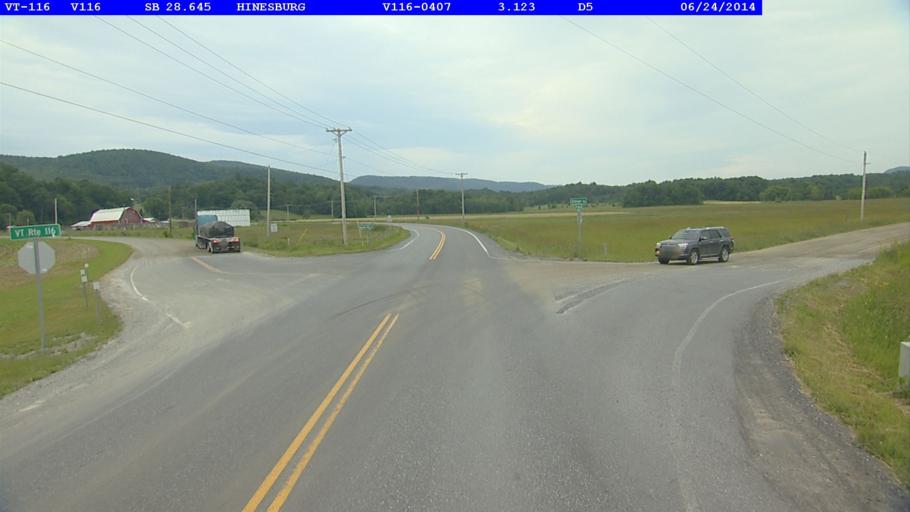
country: US
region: Vermont
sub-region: Chittenden County
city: Hinesburg
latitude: 44.3164
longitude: -73.0911
